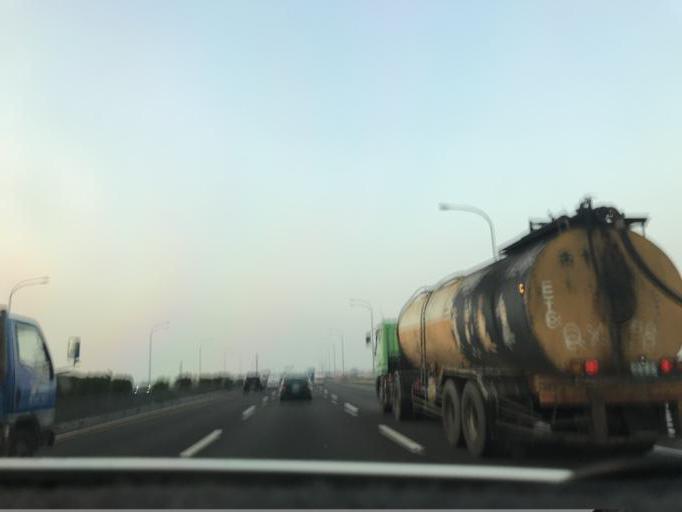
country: TW
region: Taiwan
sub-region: Yunlin
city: Douliu
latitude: 23.7324
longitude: 120.4716
